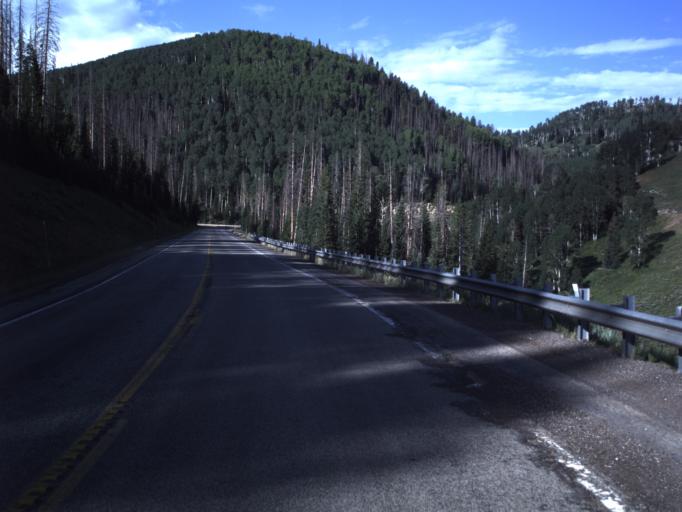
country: US
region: Utah
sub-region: Sanpete County
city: Fairview
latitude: 39.5991
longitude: -111.2186
